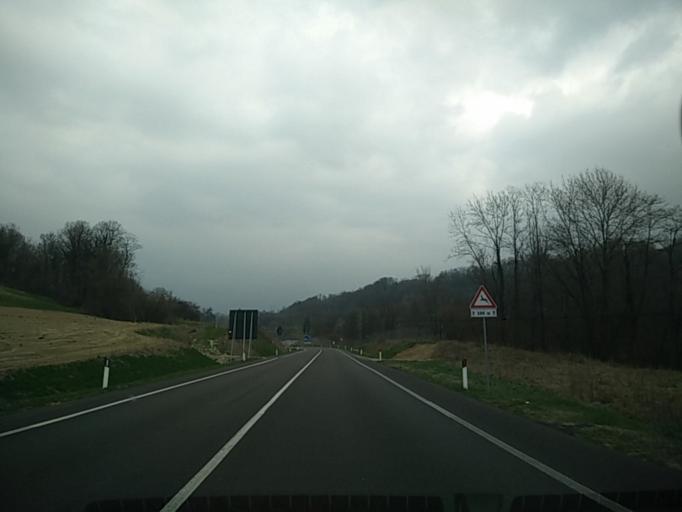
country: IT
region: Veneto
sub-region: Provincia di Belluno
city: Castion
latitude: 46.1192
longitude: 12.2076
